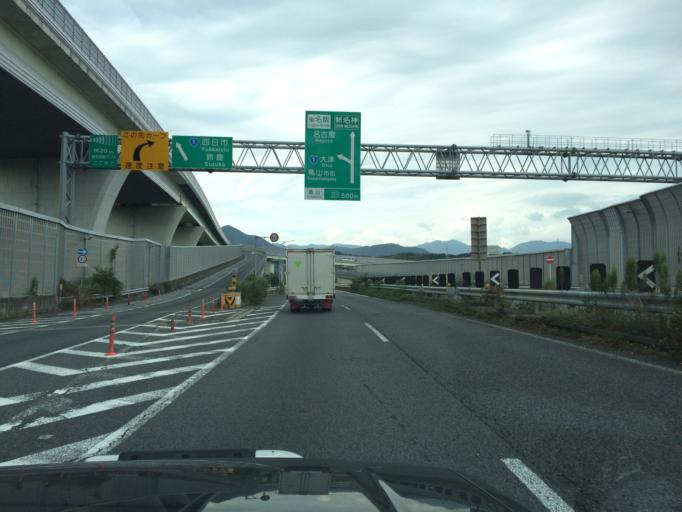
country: JP
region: Mie
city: Kameyama
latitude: 34.8534
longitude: 136.4169
